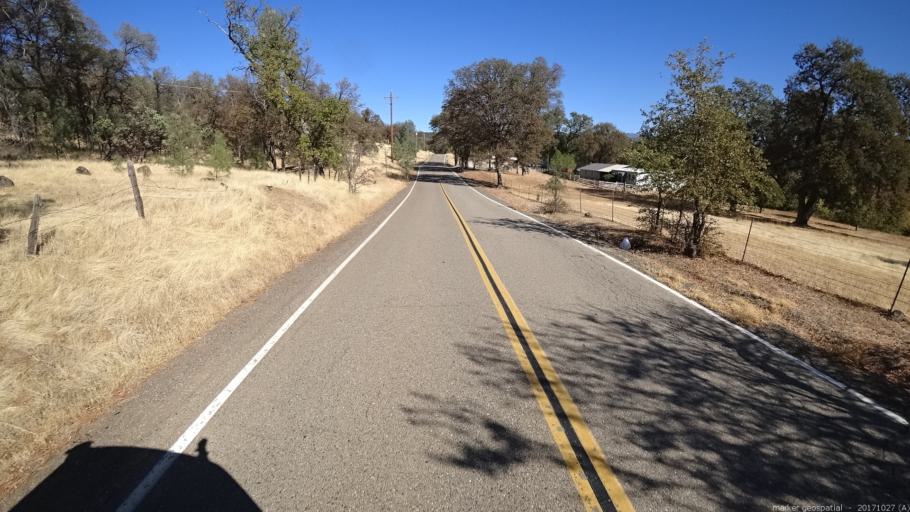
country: US
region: California
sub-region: Shasta County
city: Bella Vista
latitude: 40.6959
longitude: -122.0415
